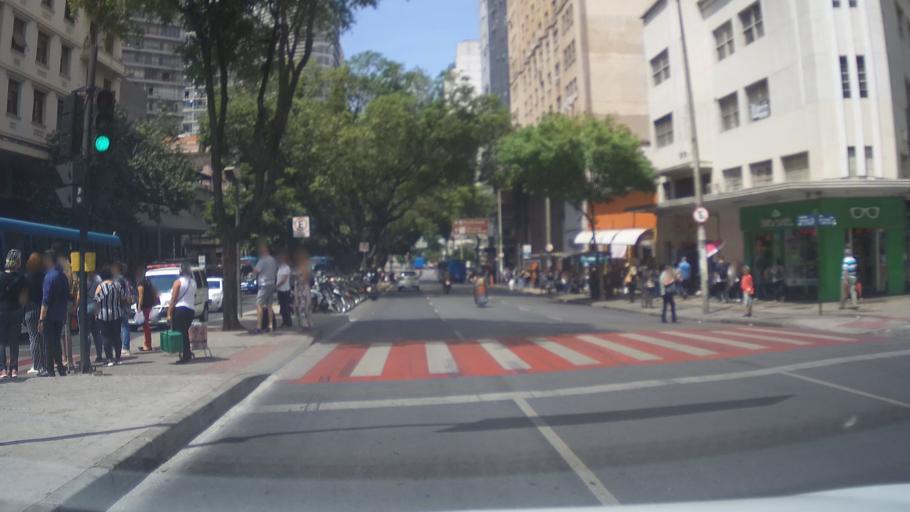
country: BR
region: Minas Gerais
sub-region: Belo Horizonte
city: Belo Horizonte
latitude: -19.9200
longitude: -43.9402
